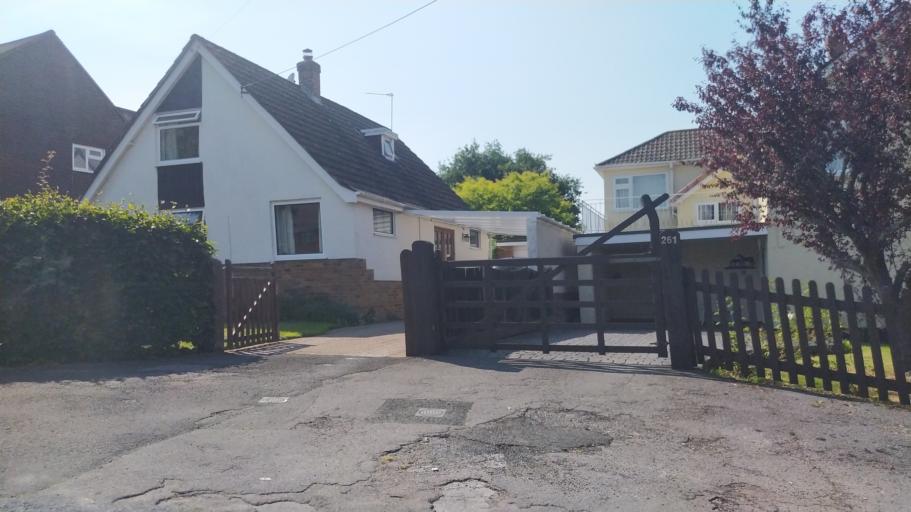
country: GB
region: England
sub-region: Hampshire
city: Cadnam
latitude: 50.9068
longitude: -1.5386
